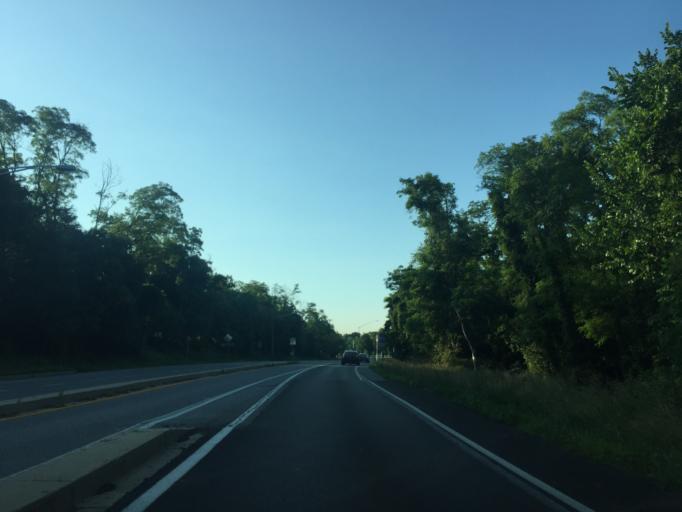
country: US
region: Maryland
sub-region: Baltimore County
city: Arbutus
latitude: 39.2490
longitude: -76.7224
